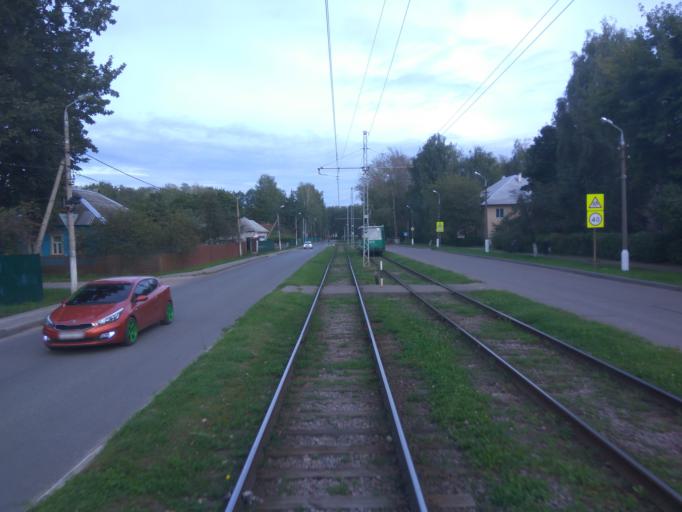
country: RU
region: Moskovskaya
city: Kolomna
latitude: 55.0751
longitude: 38.7822
